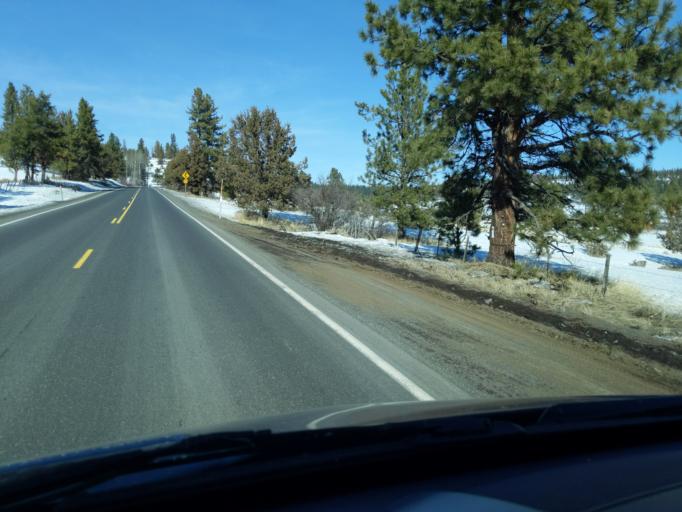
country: US
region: Oregon
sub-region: Grant County
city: John Day
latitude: 44.9004
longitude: -119.0137
